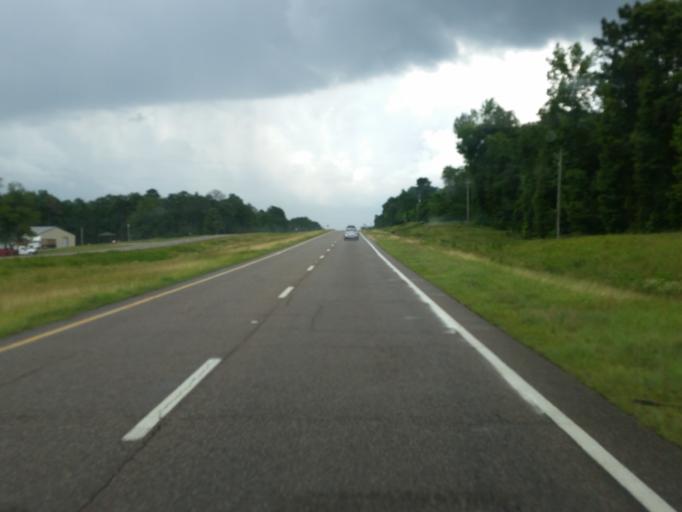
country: US
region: Mississippi
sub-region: George County
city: Lucedale
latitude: 30.9111
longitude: -88.4839
